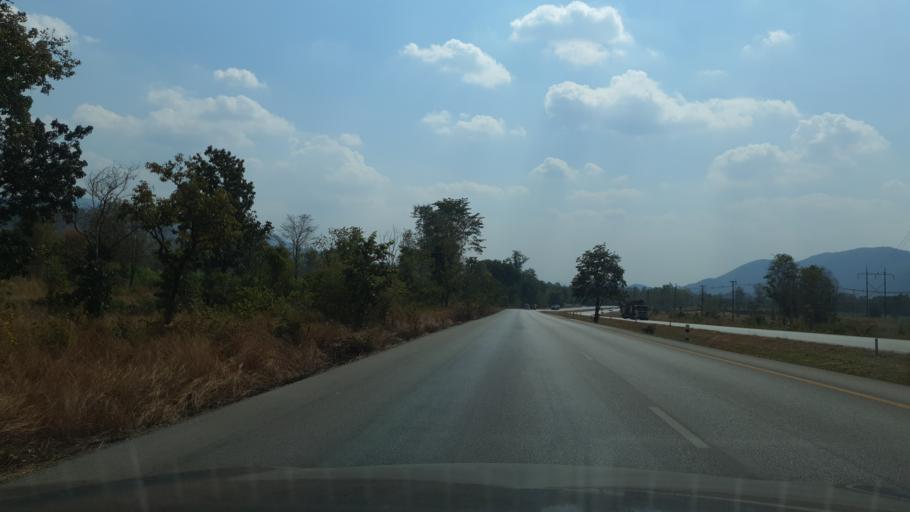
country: TH
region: Lampang
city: Mae Phrik
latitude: 17.3804
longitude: 99.1484
